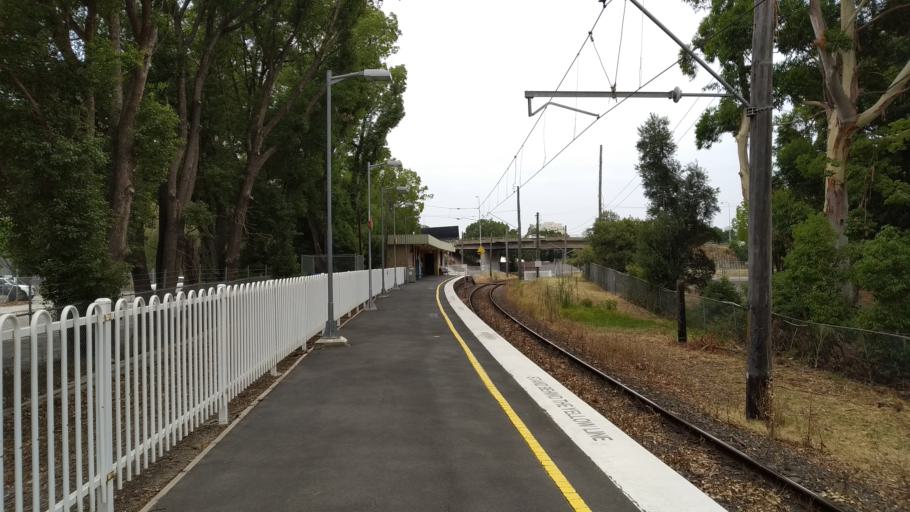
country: AU
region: New South Wales
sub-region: Parramatta
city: Granville
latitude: -33.8185
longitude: 151.0244
